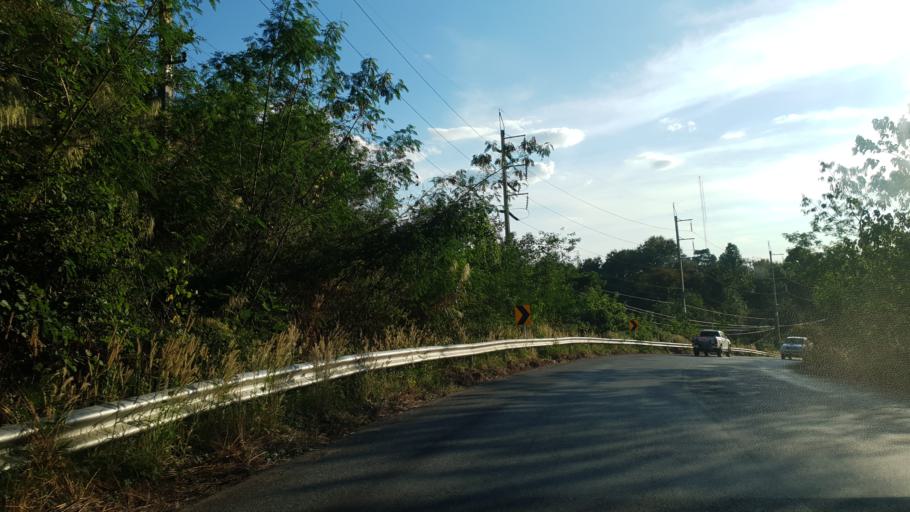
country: TH
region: Loei
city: Dan Sai
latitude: 17.2111
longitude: 101.0187
